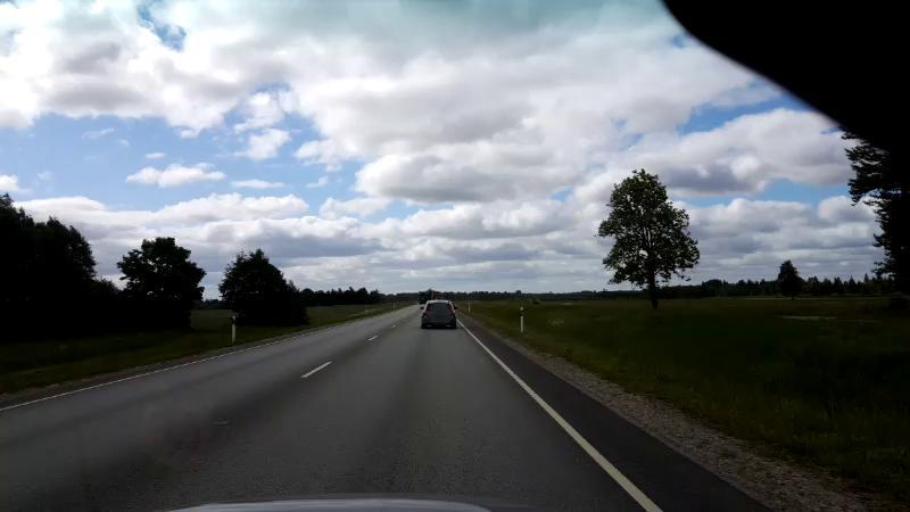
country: EE
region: Paernumaa
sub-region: Halinga vald
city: Parnu-Jaagupi
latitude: 58.5726
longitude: 24.5124
